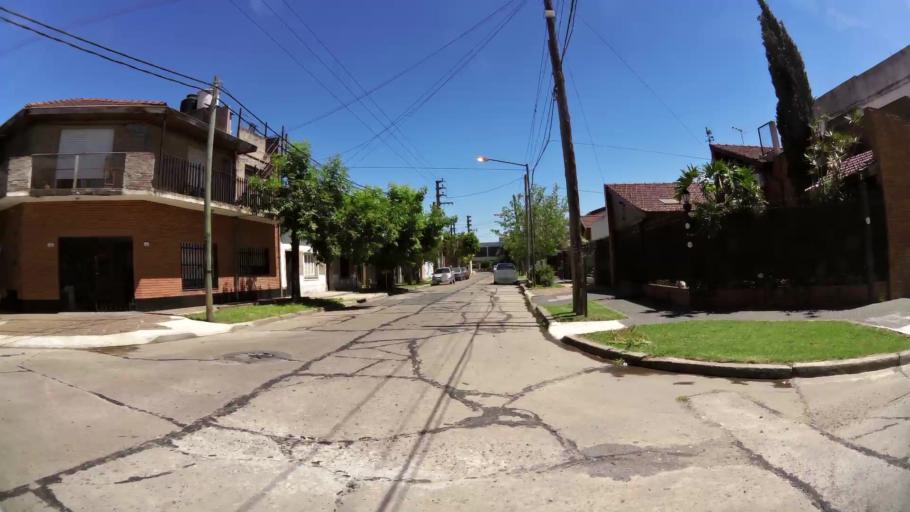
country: AR
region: Buenos Aires
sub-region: Partido de San Isidro
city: San Isidro
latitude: -34.5021
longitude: -58.5741
